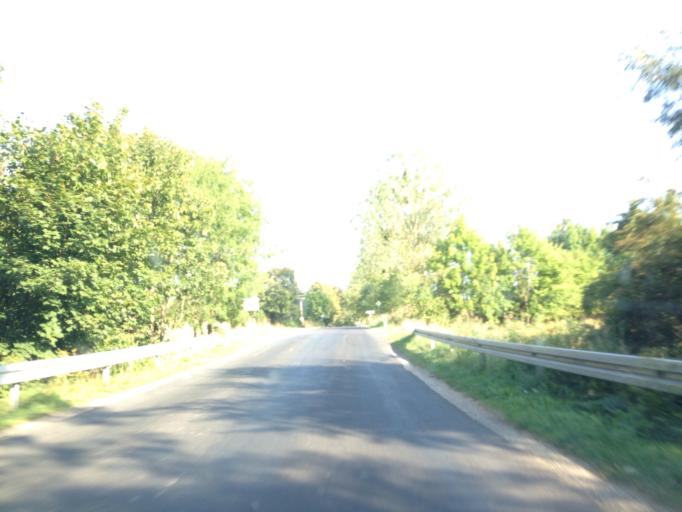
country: PL
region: Kujawsko-Pomorskie
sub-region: Powiat grudziadzki
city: Lasin
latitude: 53.5170
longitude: 19.1508
